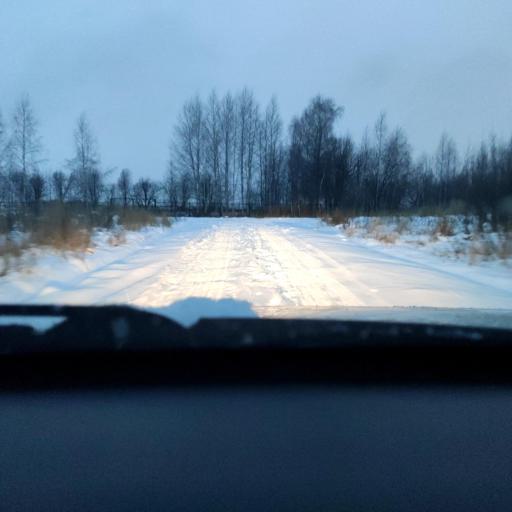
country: RU
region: Perm
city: Froly
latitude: 57.9458
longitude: 56.2313
